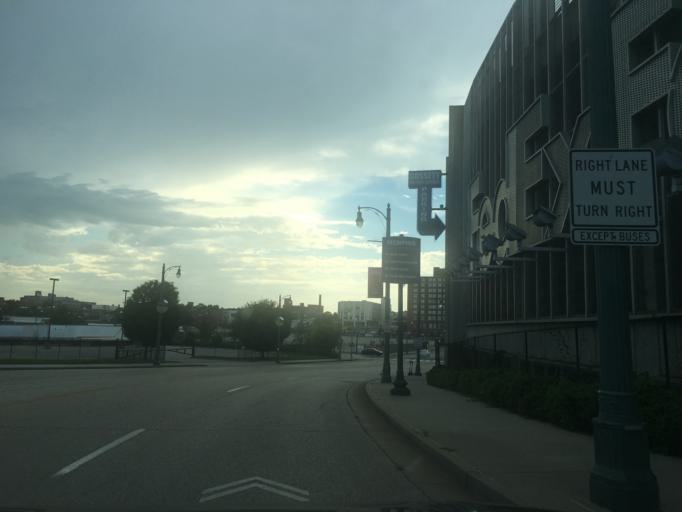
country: US
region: Tennessee
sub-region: Shelby County
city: Memphis
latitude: 35.1371
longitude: -90.0518
